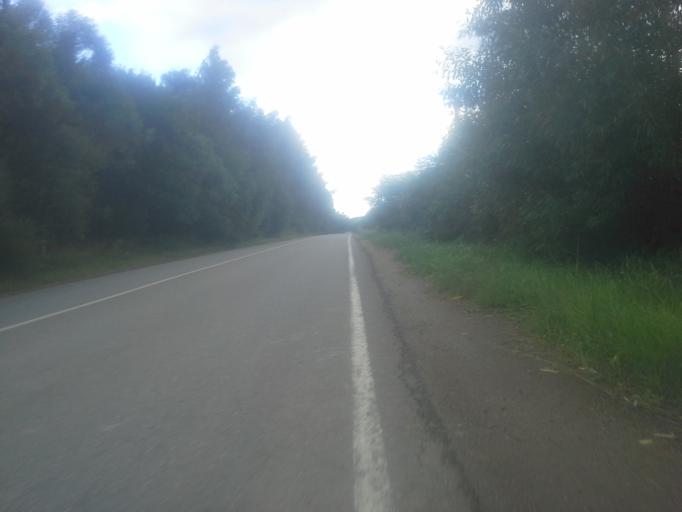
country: RU
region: Moskovskaya
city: Karinskoye
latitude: 55.6607
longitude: 36.6373
